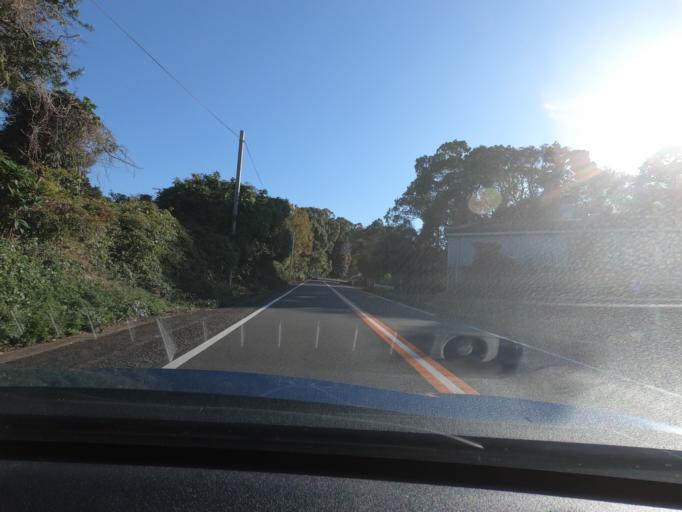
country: JP
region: Kumamoto
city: Minamata
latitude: 32.1646
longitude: 130.3753
